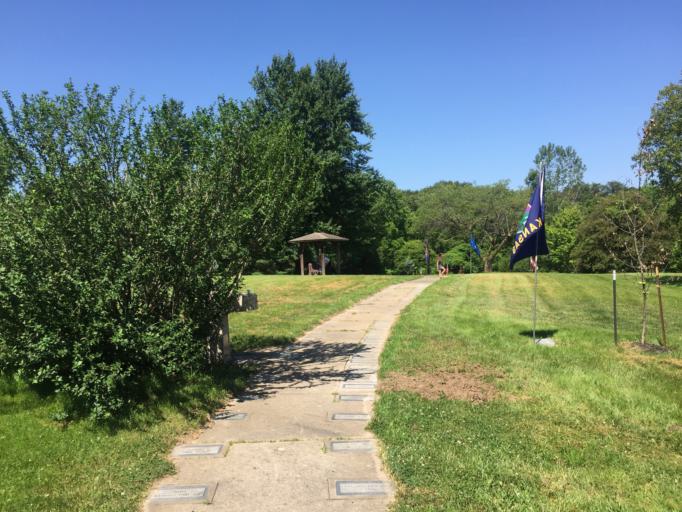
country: US
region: Kansas
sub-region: Atchison County
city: Atchison
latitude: 39.5325
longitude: -95.1488
